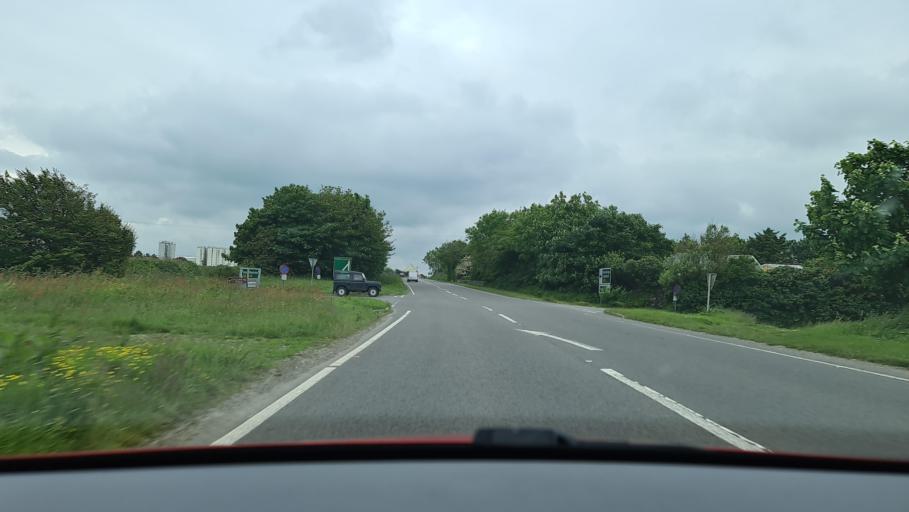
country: GB
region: England
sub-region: Cornwall
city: Camelford
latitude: 50.6536
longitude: -4.6346
